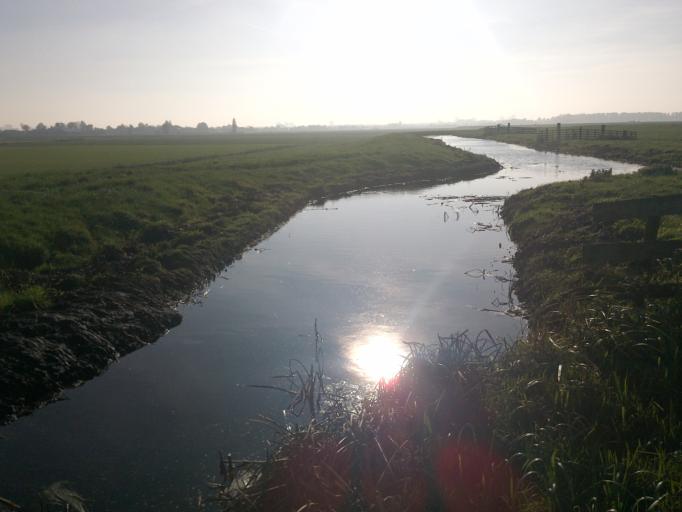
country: NL
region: South Holland
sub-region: Gemeente Rijnwoude
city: Benthuizen
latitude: 52.1025
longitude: 4.5335
